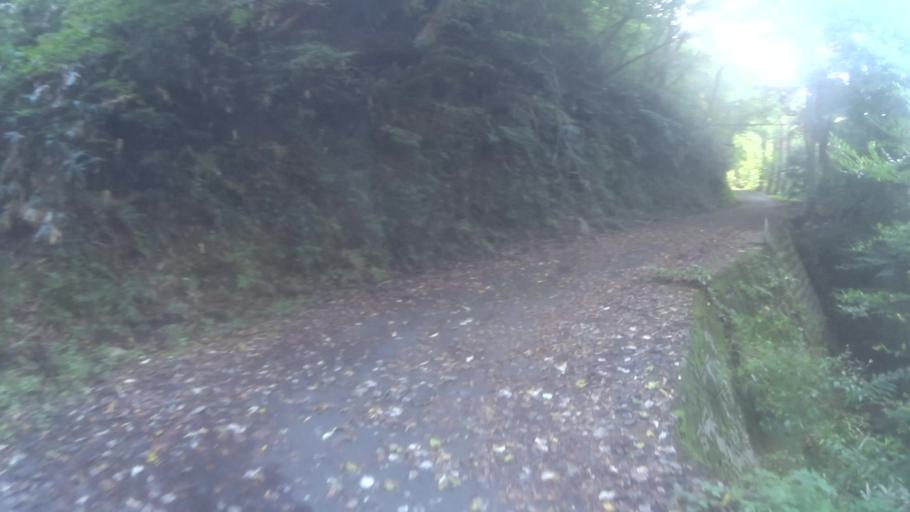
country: JP
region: Kyoto
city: Miyazu
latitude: 35.6254
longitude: 135.1599
